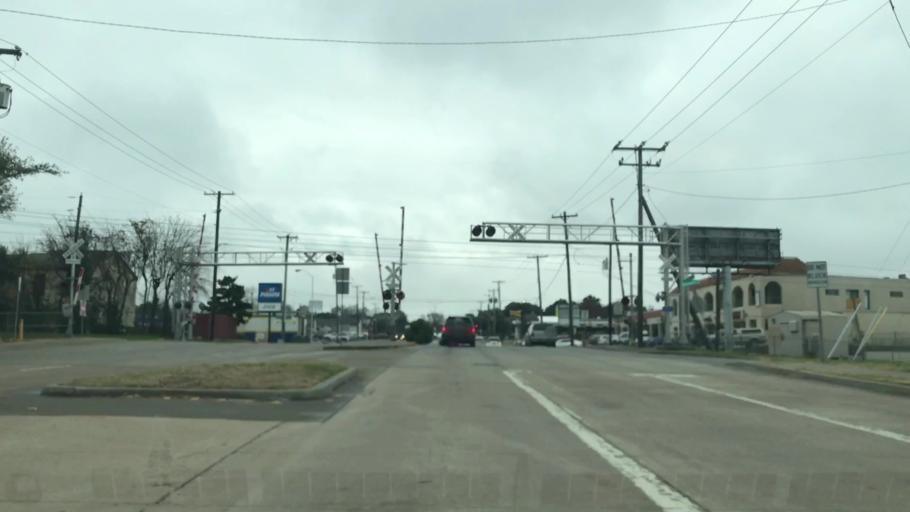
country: US
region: Texas
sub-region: Dallas County
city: Richardson
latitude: 32.8966
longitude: -96.7179
